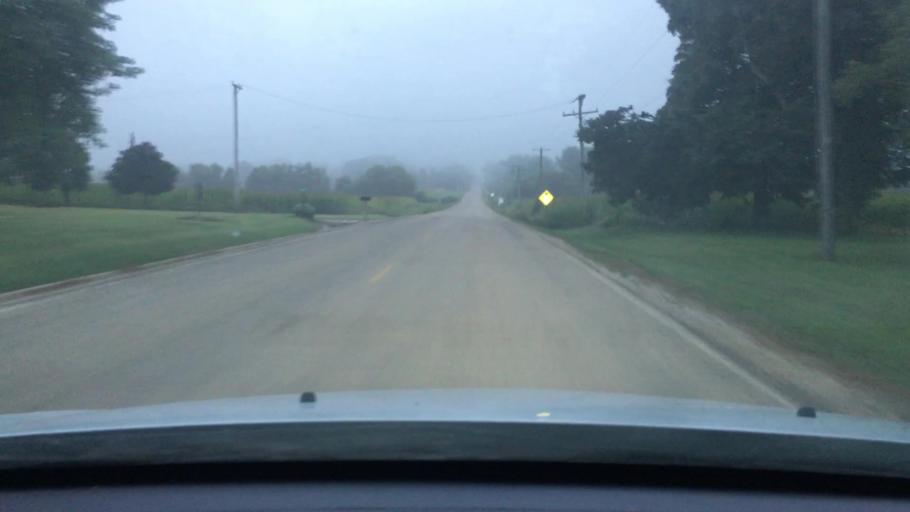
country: US
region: Illinois
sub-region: DeKalb County
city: Waterman
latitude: 41.7807
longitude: -88.7739
